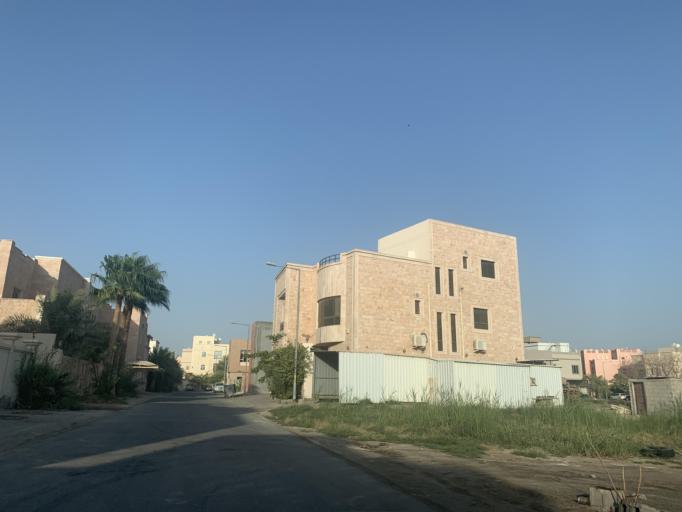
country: BH
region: Manama
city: Jidd Hafs
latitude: 26.2117
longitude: 50.5258
